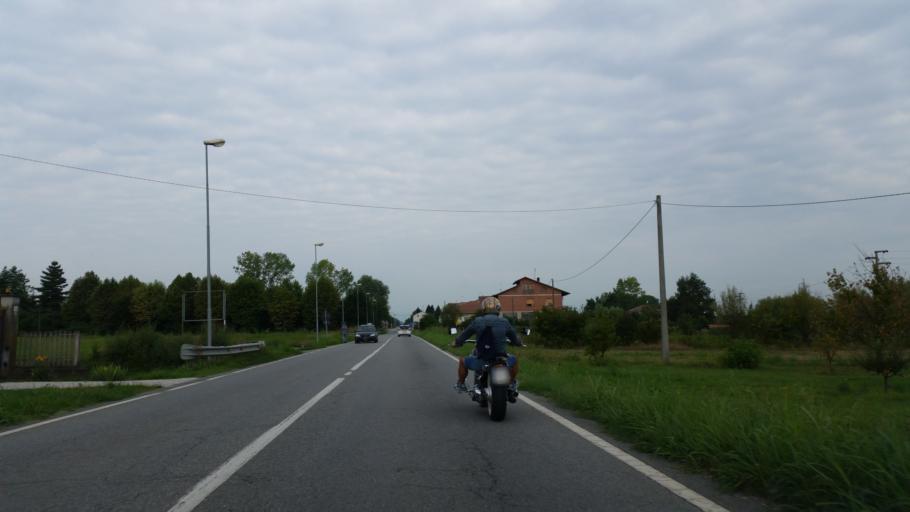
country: IT
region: Piedmont
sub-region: Provincia di Torino
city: Monteu da Po
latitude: 45.1594
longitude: 8.0258
